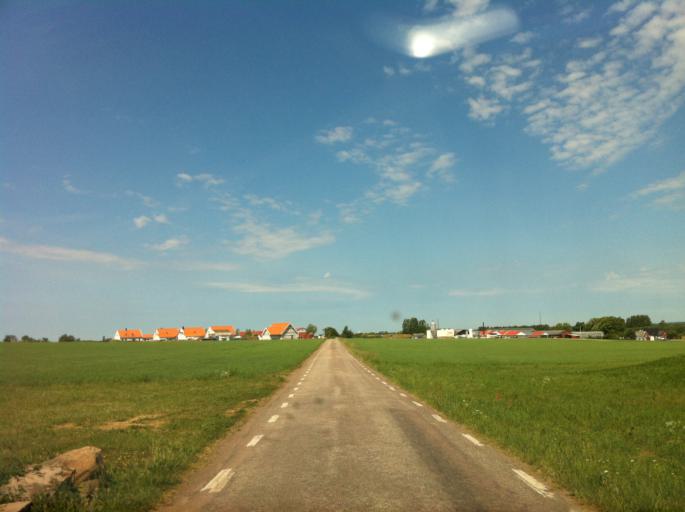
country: SE
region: Skane
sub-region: Helsingborg
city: Glumslov
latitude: 55.9441
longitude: 12.8812
